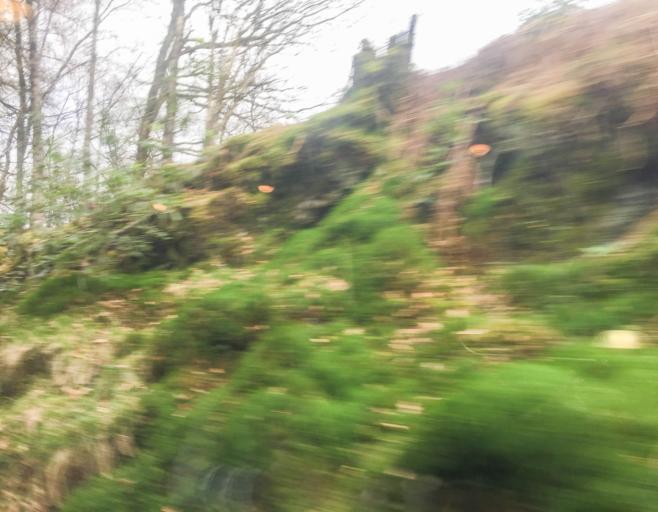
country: GB
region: Scotland
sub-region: Argyll and Bute
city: Garelochhead
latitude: 56.2182
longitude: -4.6996
